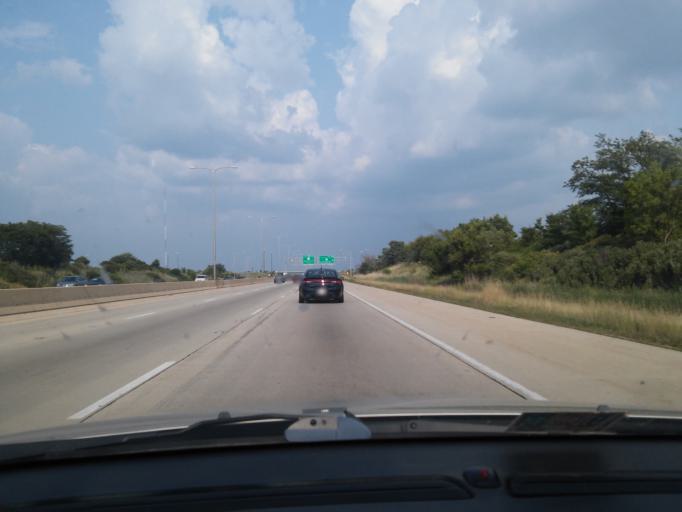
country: US
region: Illinois
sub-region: Will County
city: Mokena
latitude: 41.5527
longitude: -87.8632
